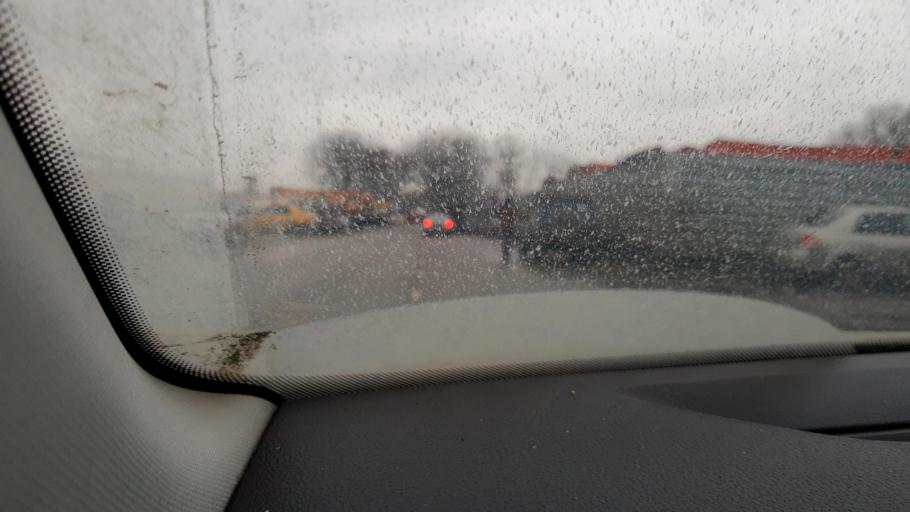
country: RU
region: Moskovskaya
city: Kur'yanovo
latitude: 55.6628
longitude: 37.7019
